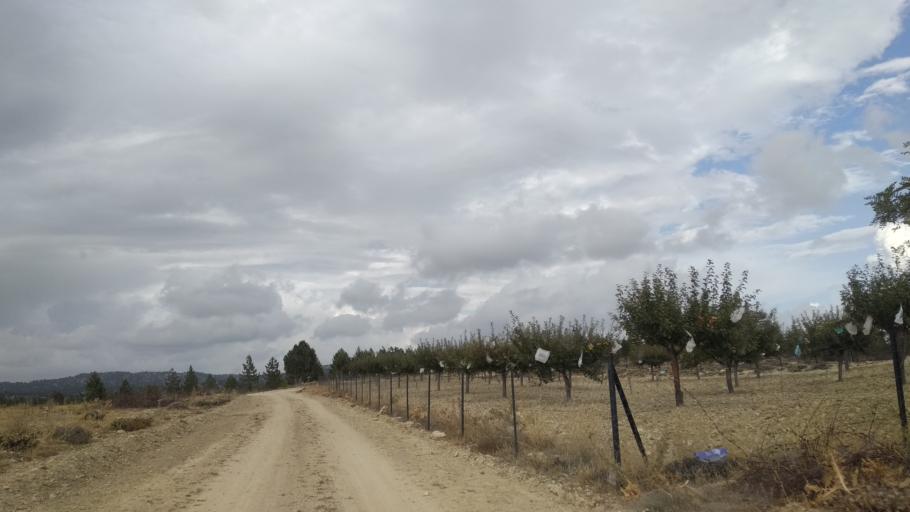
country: TR
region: Mersin
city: Sarikavak
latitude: 36.5738
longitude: 33.7569
